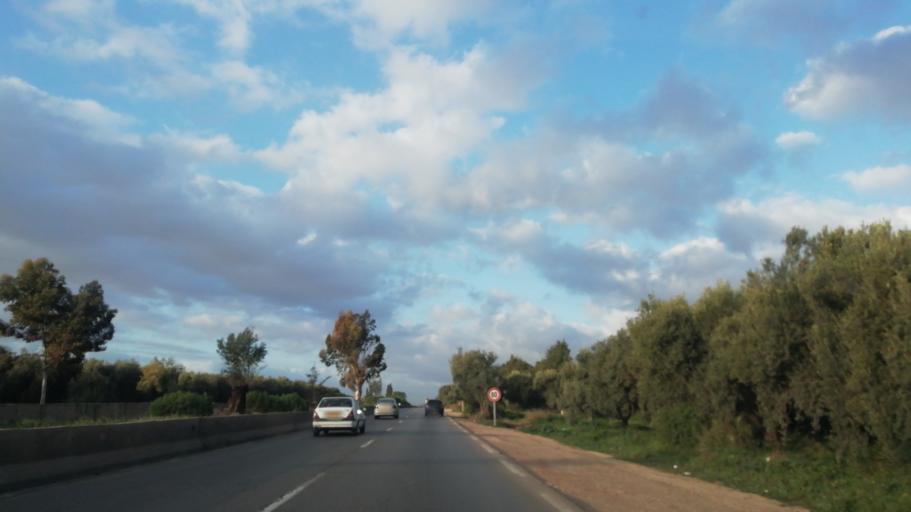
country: DZ
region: Oran
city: Bou Tlelis
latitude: 35.5925
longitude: -0.7940
